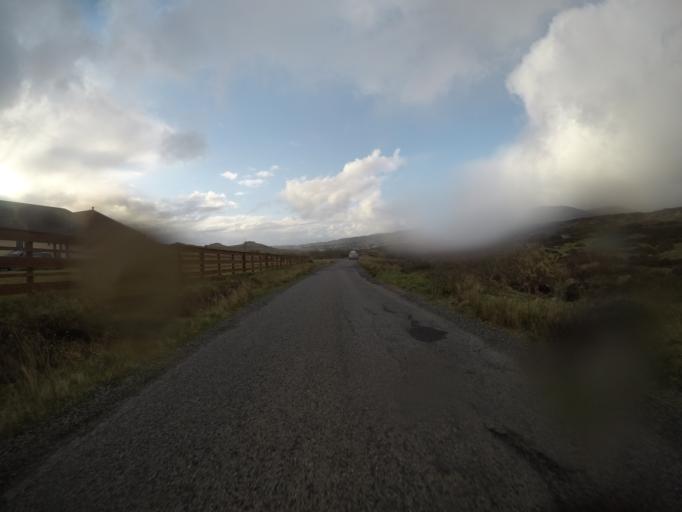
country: GB
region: Scotland
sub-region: Highland
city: Isle of Skye
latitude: 57.4668
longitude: -6.2984
